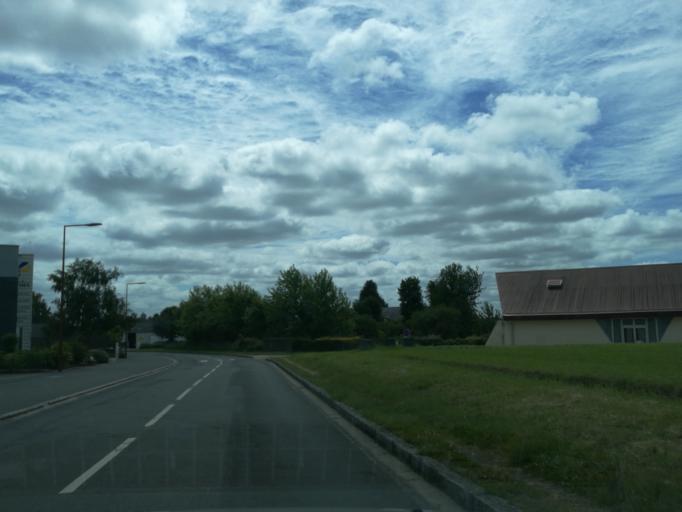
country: FR
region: Brittany
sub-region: Departement d'Ille-et-Vilaine
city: Bedee
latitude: 48.1823
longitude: -1.9372
